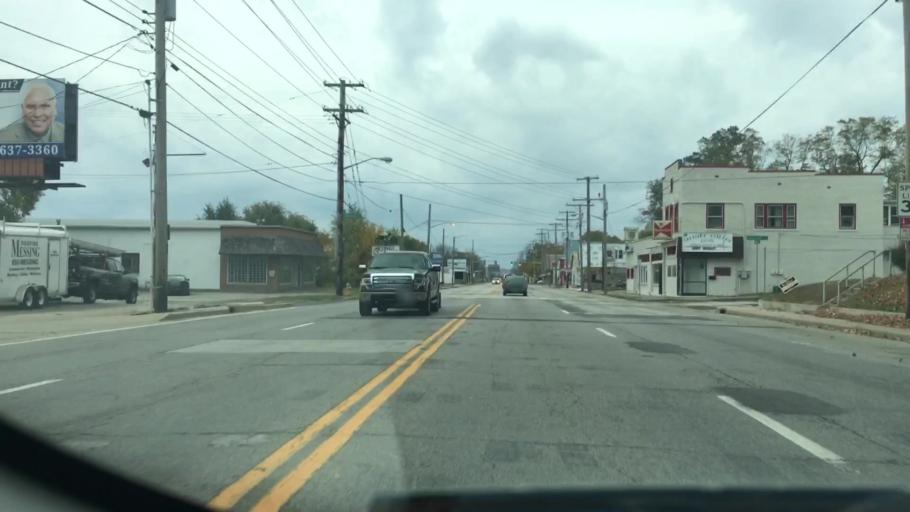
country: US
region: Illinois
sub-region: Peoria County
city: North Peoria
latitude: 40.7195
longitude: -89.5577
